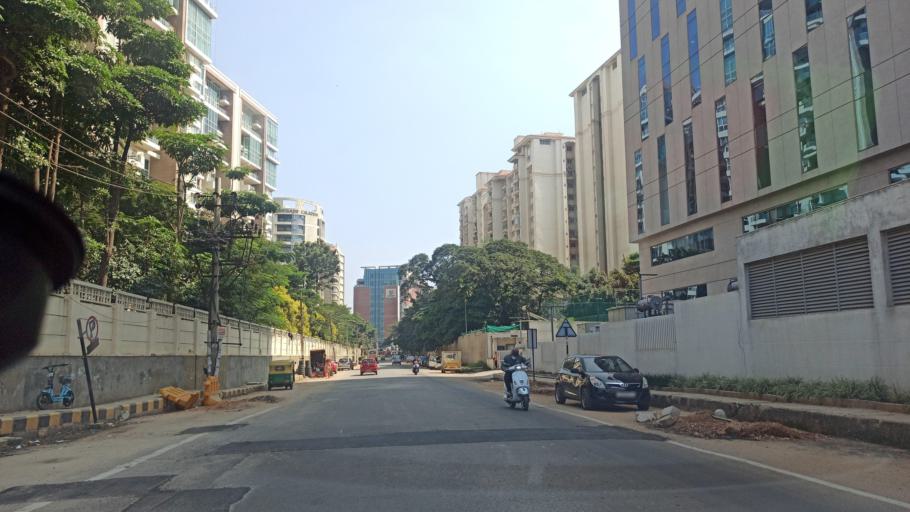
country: IN
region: Karnataka
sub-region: Bangalore Urban
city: Yelahanka
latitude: 13.0557
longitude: 77.5941
